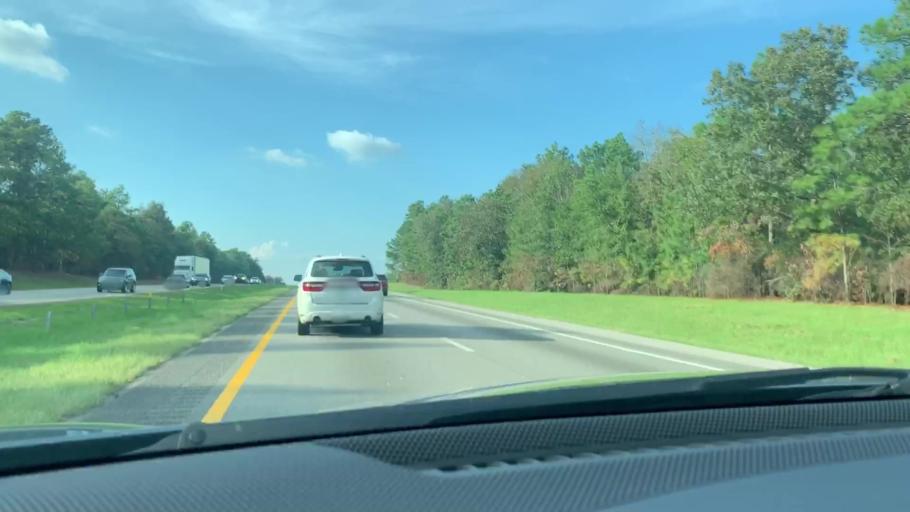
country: US
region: South Carolina
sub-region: Calhoun County
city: Oak Grove
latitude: 33.7320
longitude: -80.9327
